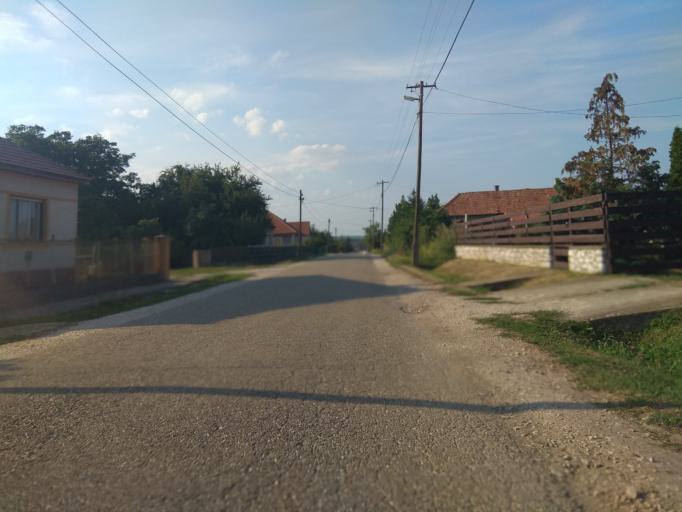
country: HU
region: Borsod-Abauj-Zemplen
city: Harsany
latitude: 47.9164
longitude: 20.7407
